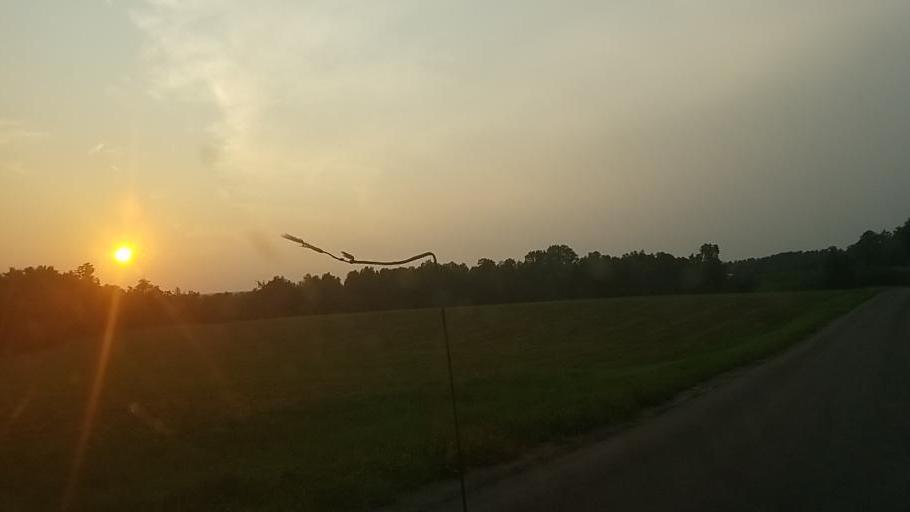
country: US
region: New York
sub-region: Montgomery County
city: Fonda
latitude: 42.9073
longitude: -74.3941
